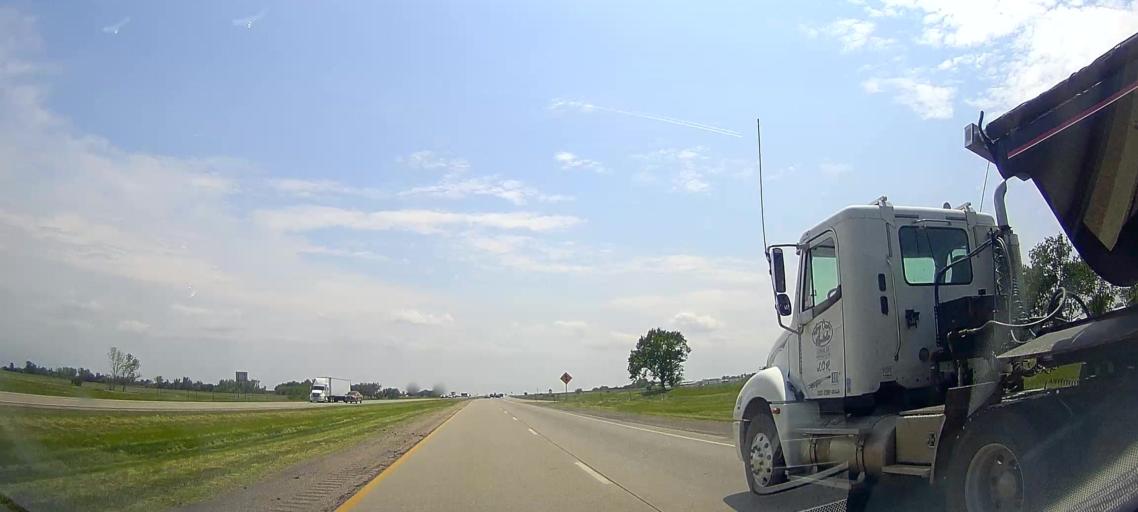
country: US
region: South Dakota
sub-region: Lincoln County
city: Tea
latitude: 43.4304
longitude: -96.7964
